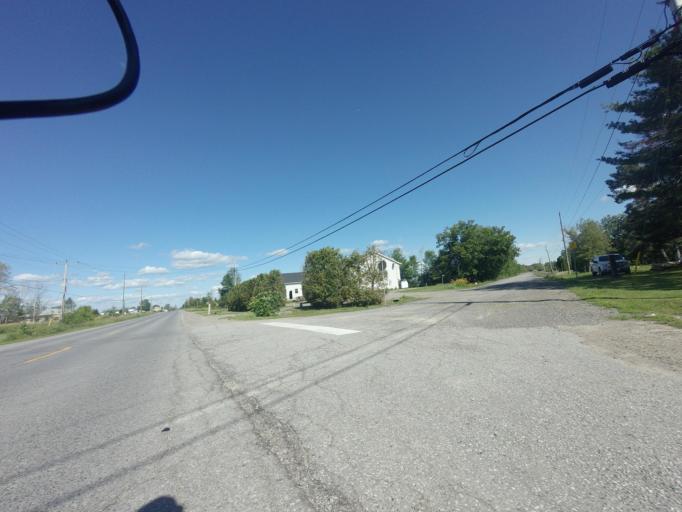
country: CA
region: Ontario
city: Arnprior
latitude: 45.4175
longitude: -76.4060
